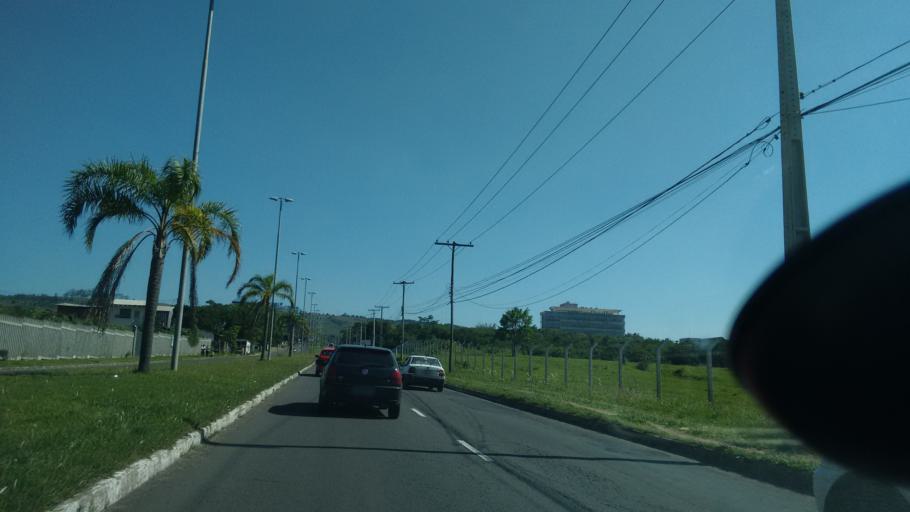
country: BR
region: Rio Grande do Sul
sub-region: Cachoeirinha
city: Cachoeirinha
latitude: -30.0288
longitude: -51.1207
